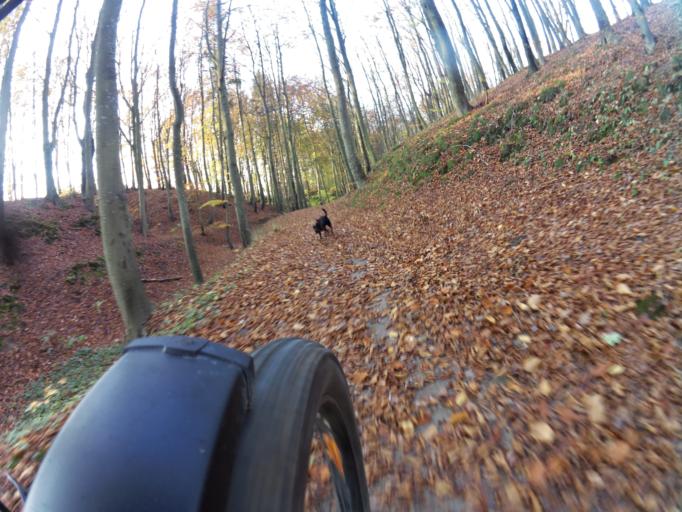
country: PL
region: Pomeranian Voivodeship
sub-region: Powiat pucki
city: Krokowa
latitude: 54.7703
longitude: 18.1754
